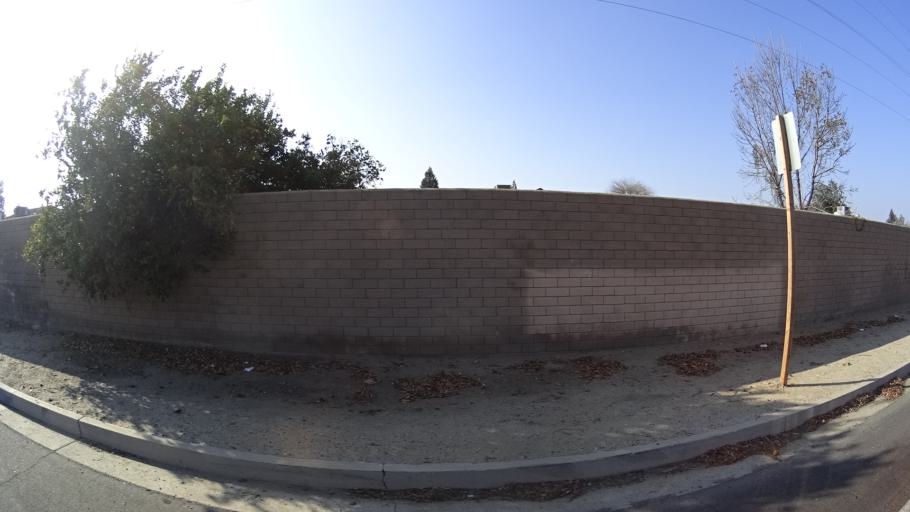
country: US
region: California
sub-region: Kern County
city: Oildale
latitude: 35.4133
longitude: -119.0129
